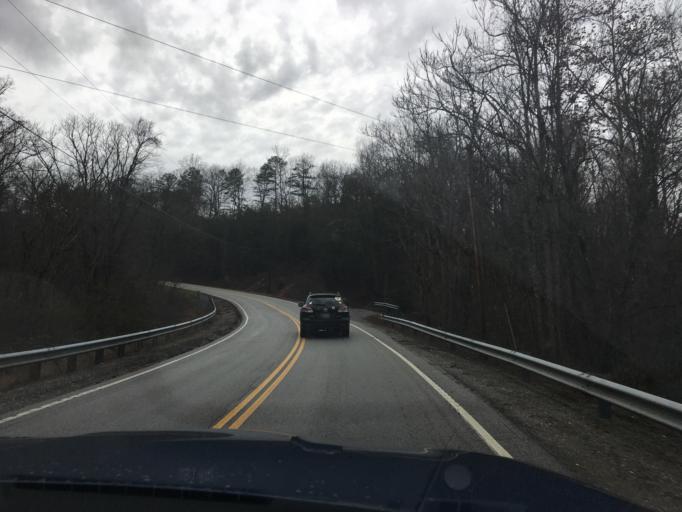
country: US
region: Tennessee
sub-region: McMinn County
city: Englewood
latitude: 35.3423
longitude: -84.3770
